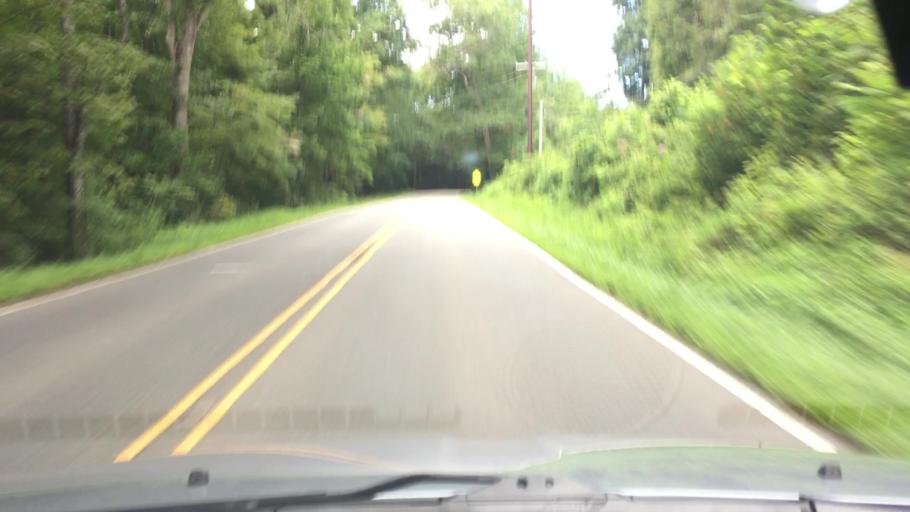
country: US
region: North Carolina
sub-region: Yancey County
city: Burnsville
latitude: 35.8342
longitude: -82.1862
